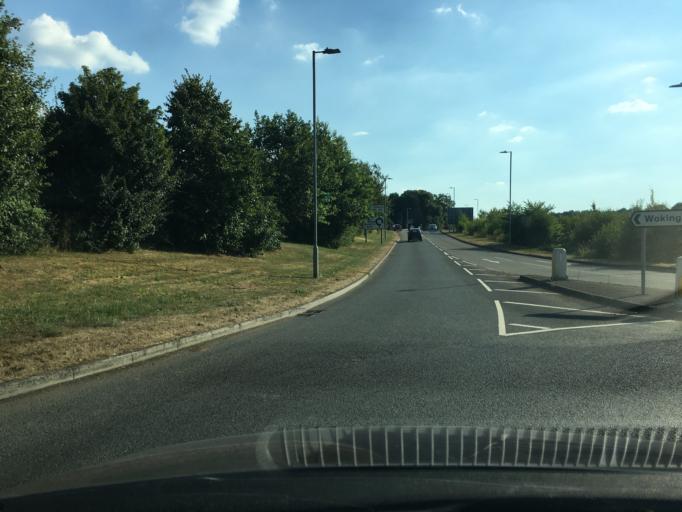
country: GB
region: England
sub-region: Bracknell Forest
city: Binfield
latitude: 51.4088
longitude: -0.7851
